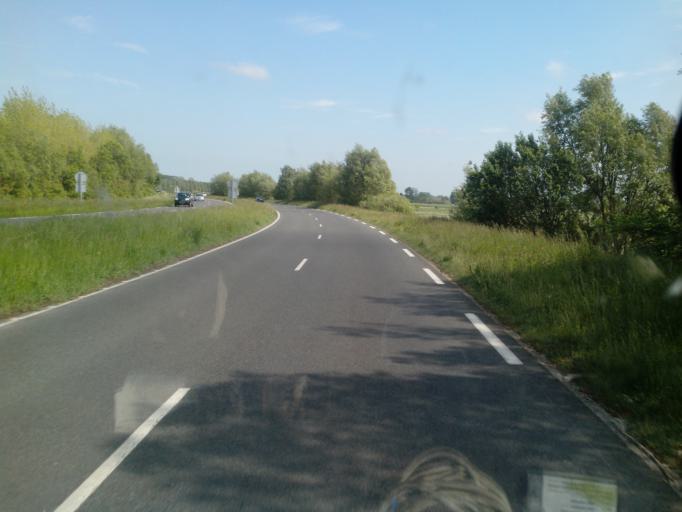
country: FR
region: Picardie
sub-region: Departement de la Somme
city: Quend
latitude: 50.3055
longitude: 1.6372
